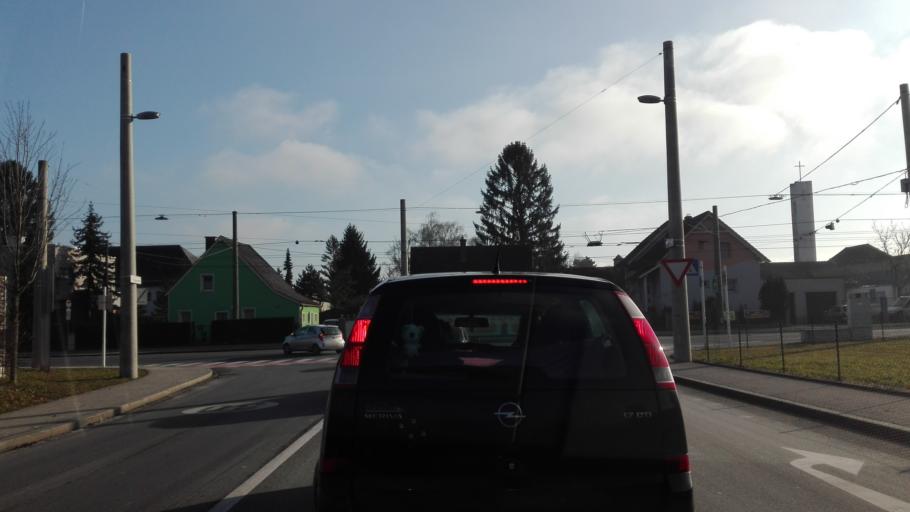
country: AT
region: Upper Austria
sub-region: Politischer Bezirk Linz-Land
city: Leonding
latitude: 48.2570
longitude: 14.2878
